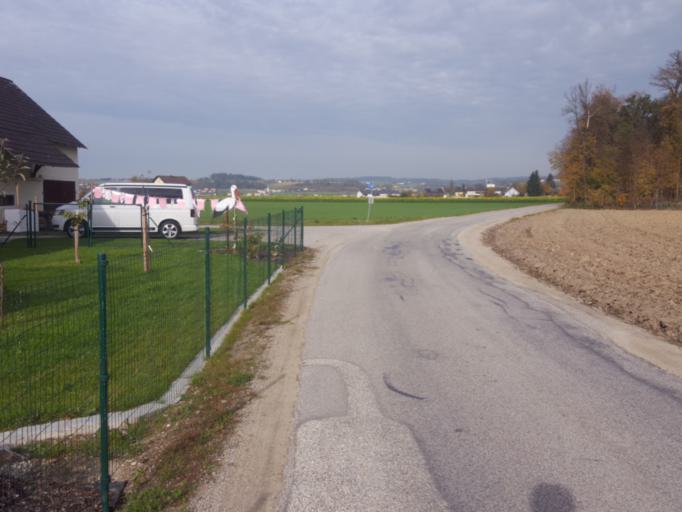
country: AT
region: Upper Austria
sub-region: Politischer Bezirk Perg
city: Perg
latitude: 48.2509
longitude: 14.5690
